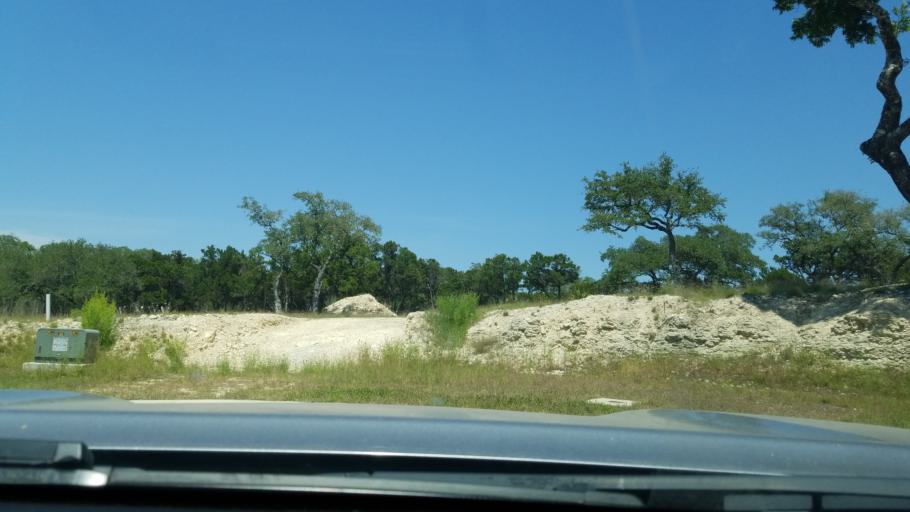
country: US
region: Texas
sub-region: Kendall County
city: Boerne
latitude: 29.7943
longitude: -98.6922
